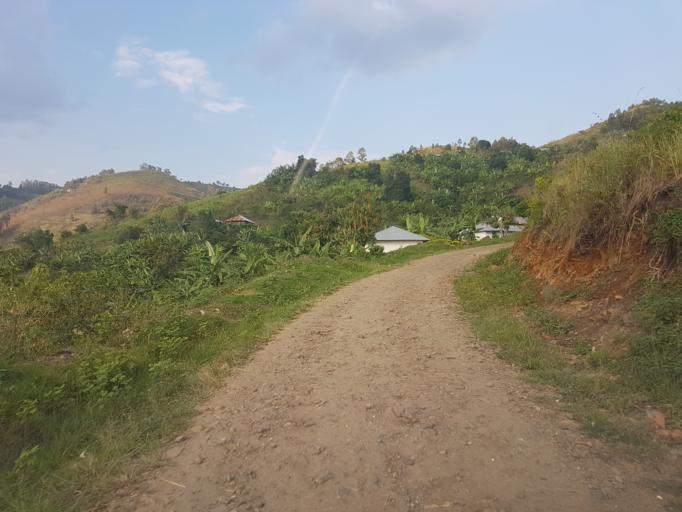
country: UG
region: Western Region
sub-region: Mitoma District
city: Mitoma
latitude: -0.6773
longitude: 29.9022
